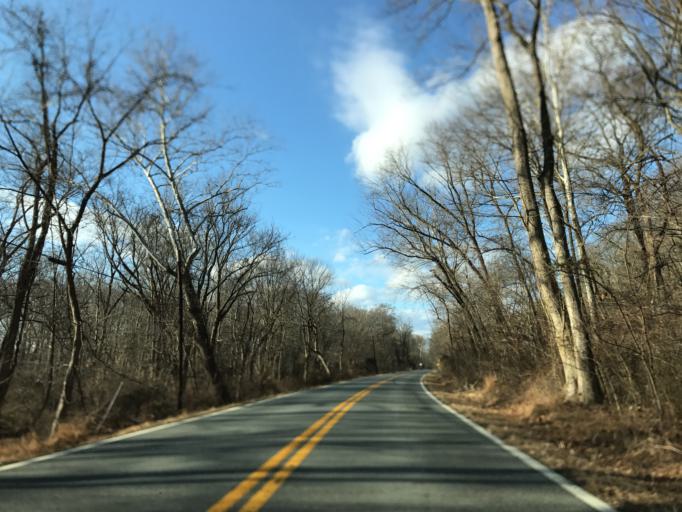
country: US
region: Maryland
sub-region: Harford County
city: Havre de Grace
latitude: 39.6228
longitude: -76.1381
